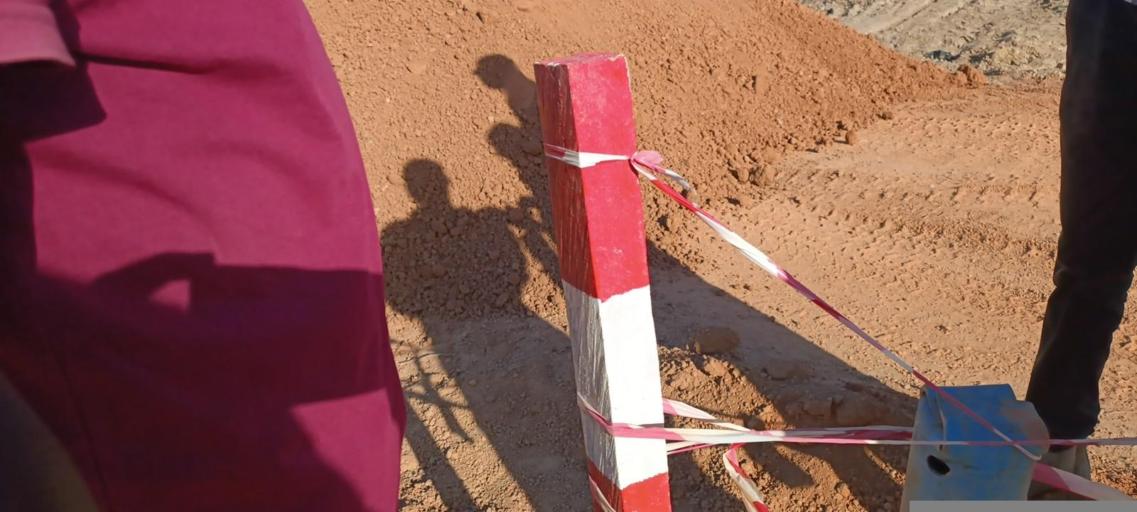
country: BF
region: Est
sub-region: Province du Gourma
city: Fada N'gourma
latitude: 12.0551
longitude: 0.3425
